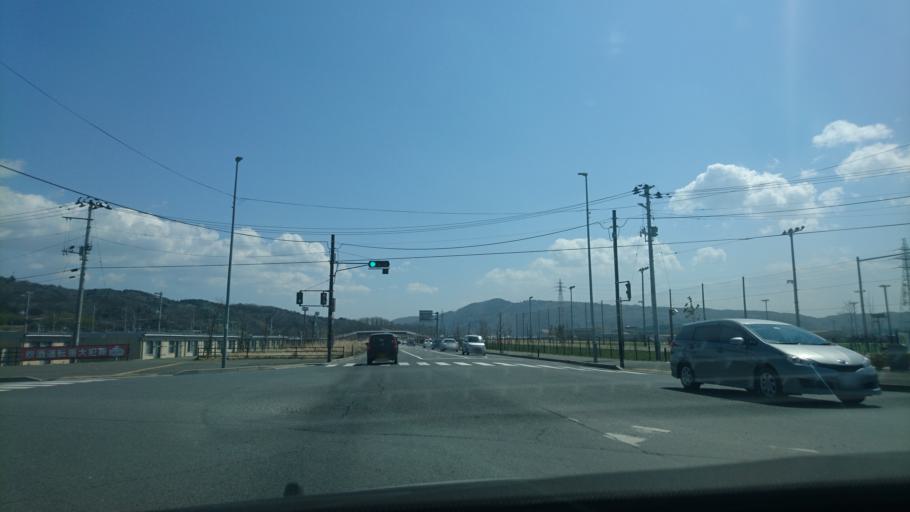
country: JP
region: Miyagi
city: Ishinomaki
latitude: 38.4557
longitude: 141.3020
